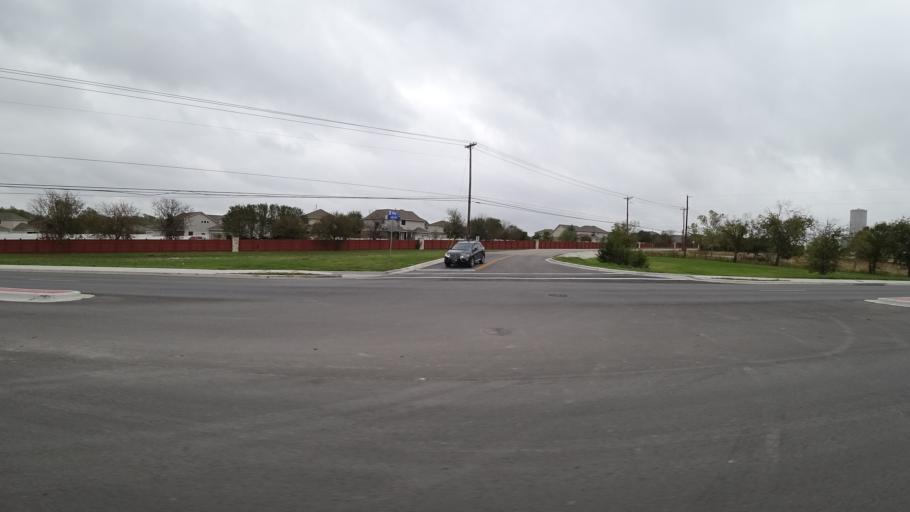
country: US
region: Texas
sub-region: Travis County
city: Windemere
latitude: 30.4702
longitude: -97.6227
